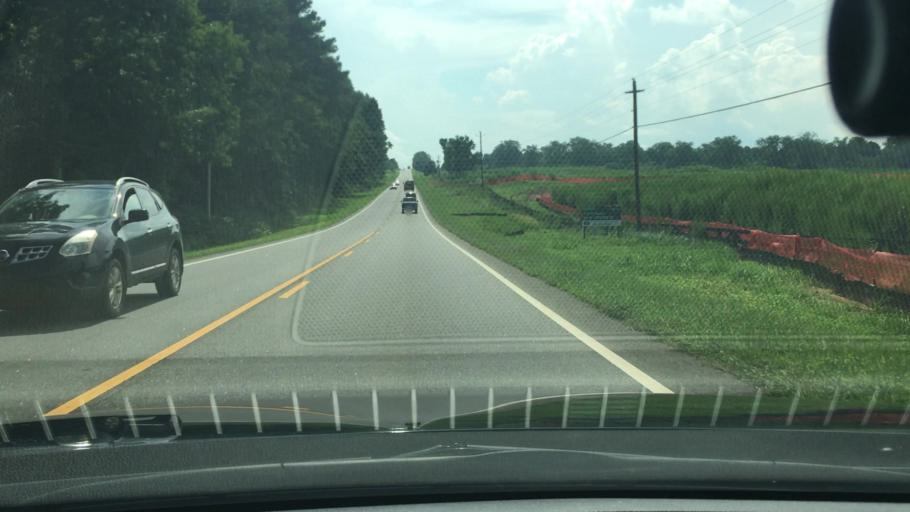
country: US
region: Georgia
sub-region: Coweta County
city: East Newnan
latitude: 33.3321
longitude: -84.7624
